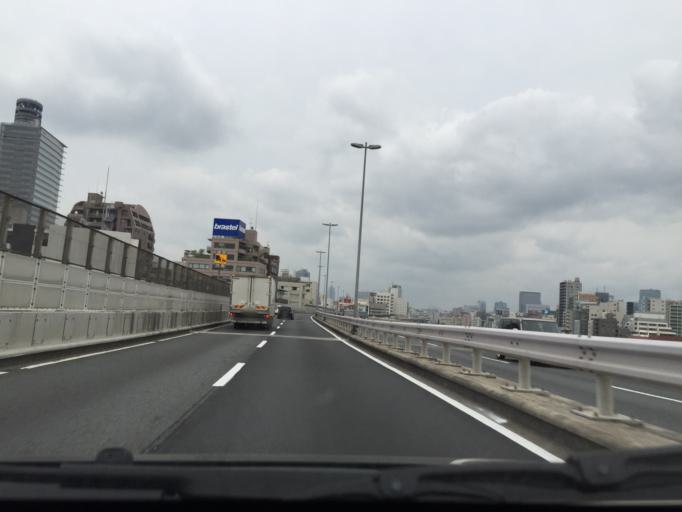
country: JP
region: Tokyo
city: Urayasu
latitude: 35.7027
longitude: 139.7951
